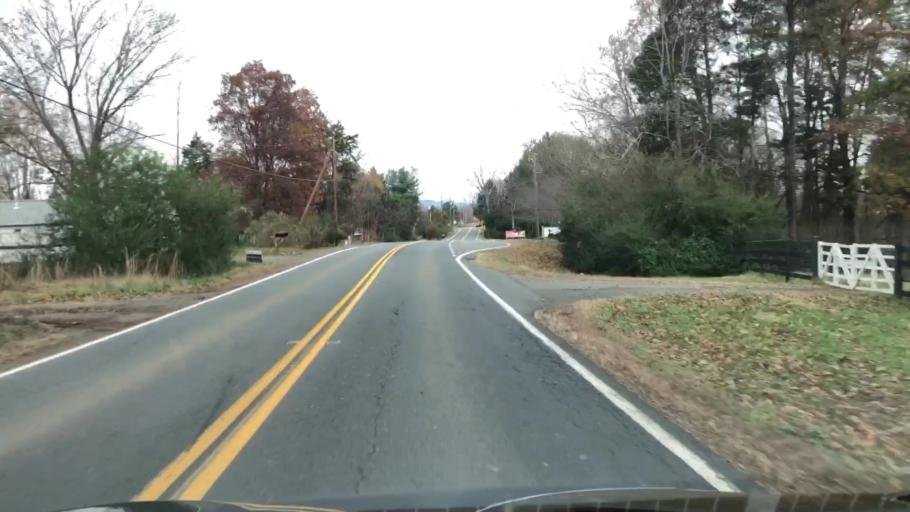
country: US
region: Virginia
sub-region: Fauquier County
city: New Baltimore
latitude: 38.7739
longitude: -77.6817
